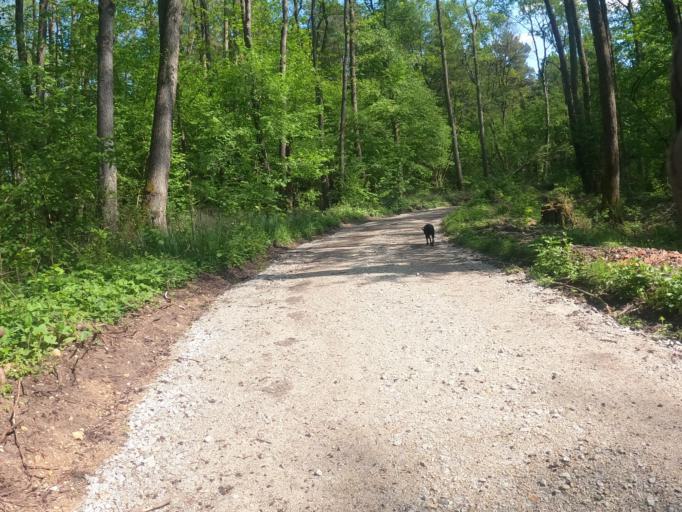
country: PL
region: West Pomeranian Voivodeship
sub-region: Powiat mysliborski
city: Barlinek
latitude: 53.0157
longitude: 15.2444
